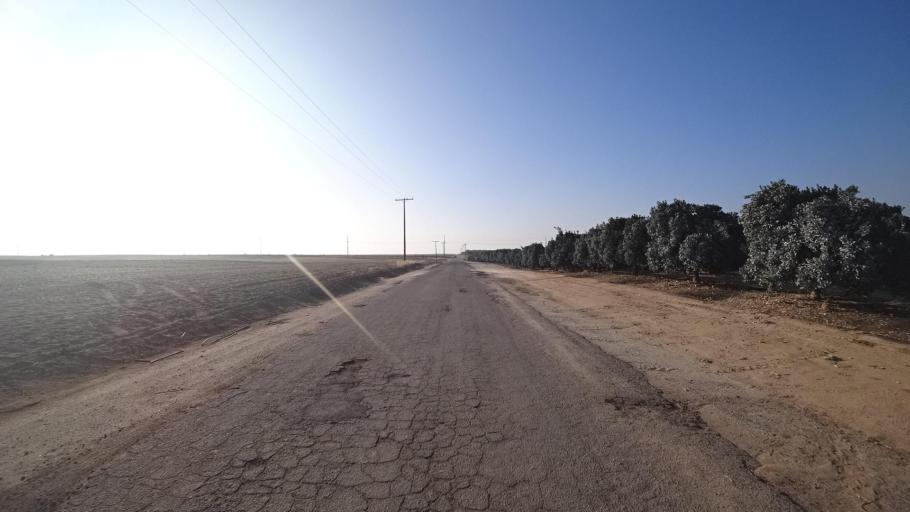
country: US
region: California
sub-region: Tulare County
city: Richgrove
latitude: 35.7644
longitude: -119.0805
